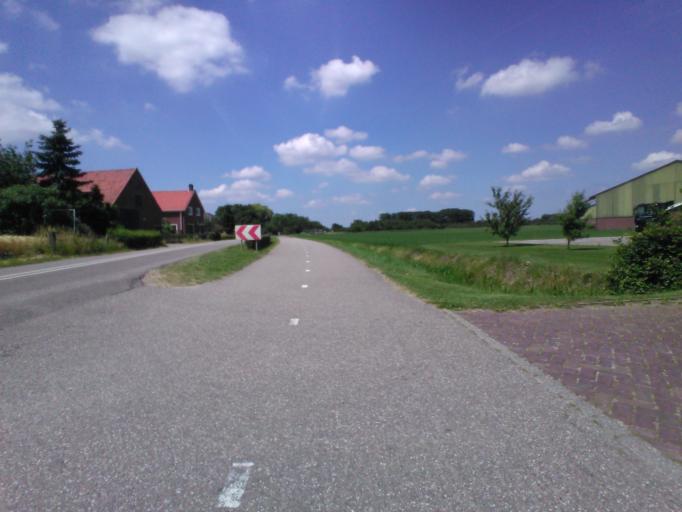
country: NL
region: North Brabant
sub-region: Gemeente Woudrichem
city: Woudrichem
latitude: 51.8079
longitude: 4.9756
